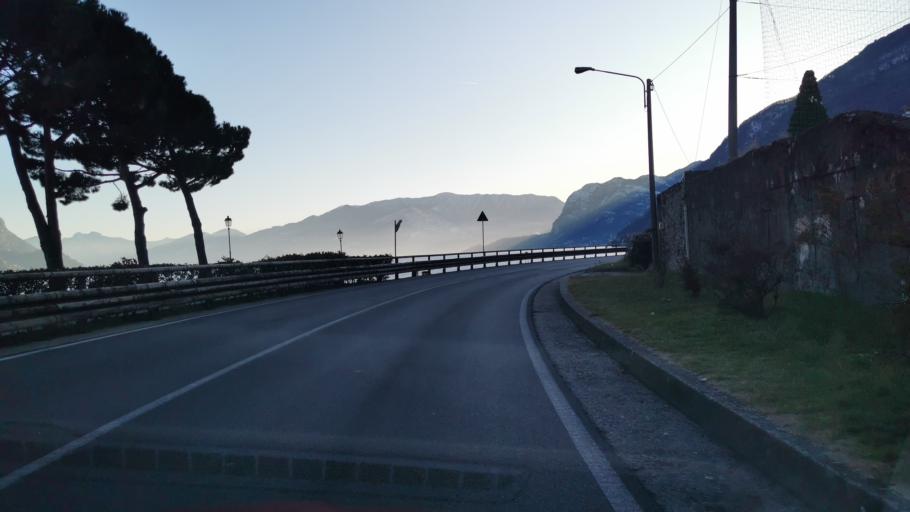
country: IT
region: Lombardy
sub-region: Provincia di Como
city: San Siro
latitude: 46.0630
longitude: 9.2690
